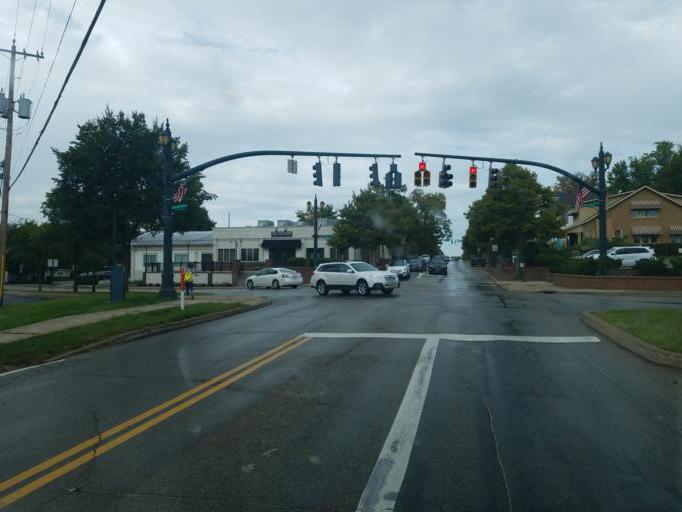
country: US
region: Ohio
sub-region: Franklin County
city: New Albany
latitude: 40.0813
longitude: -82.8088
